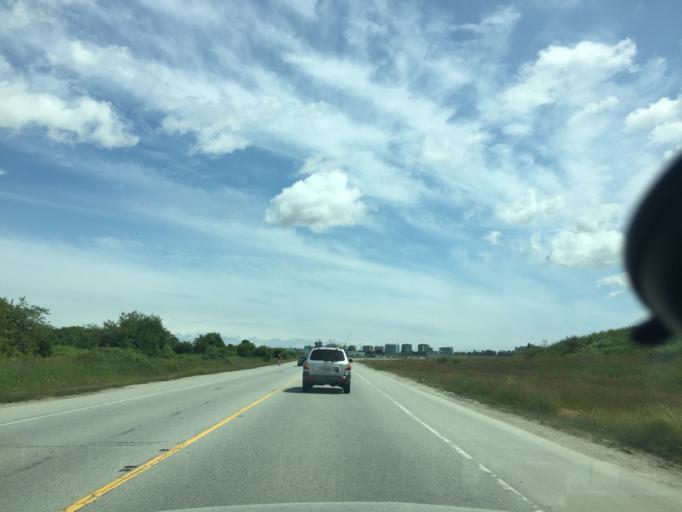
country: CA
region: British Columbia
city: Richmond
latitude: 49.2030
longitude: -123.1519
